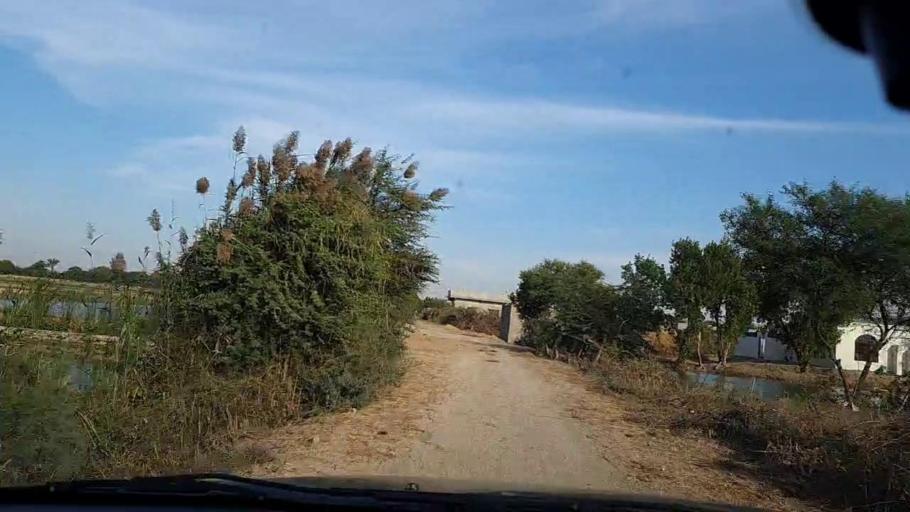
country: PK
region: Sindh
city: Mirpur Batoro
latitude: 24.6520
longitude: 68.2949
